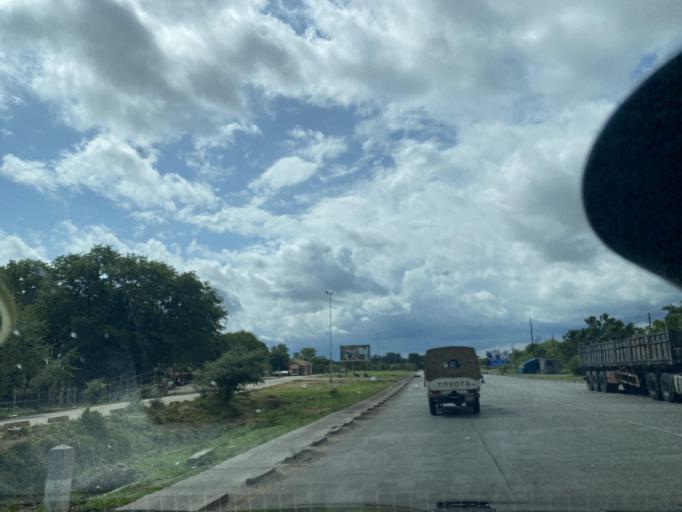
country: ZM
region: Lusaka
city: Kafue
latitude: -15.8462
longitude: 28.2447
